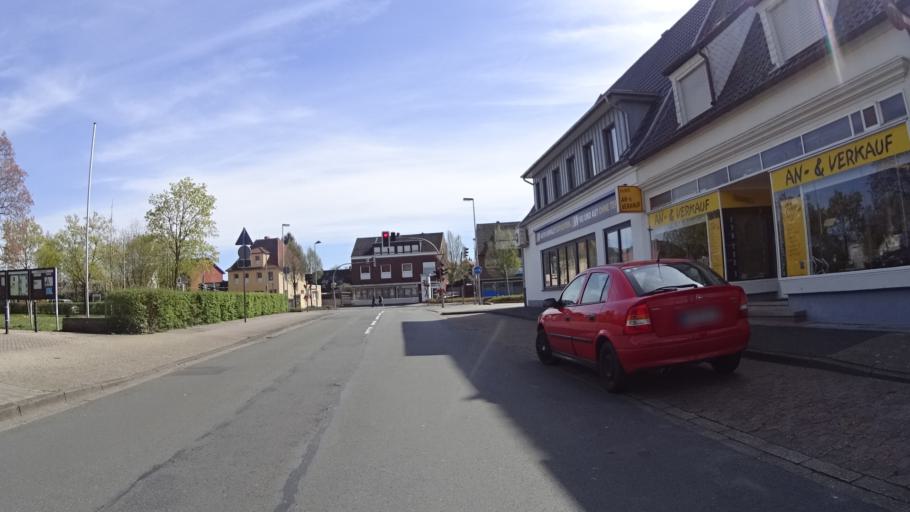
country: DE
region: North Rhine-Westphalia
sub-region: Regierungsbezirk Munster
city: Dreierwalde
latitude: 52.2868
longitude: 7.4746
